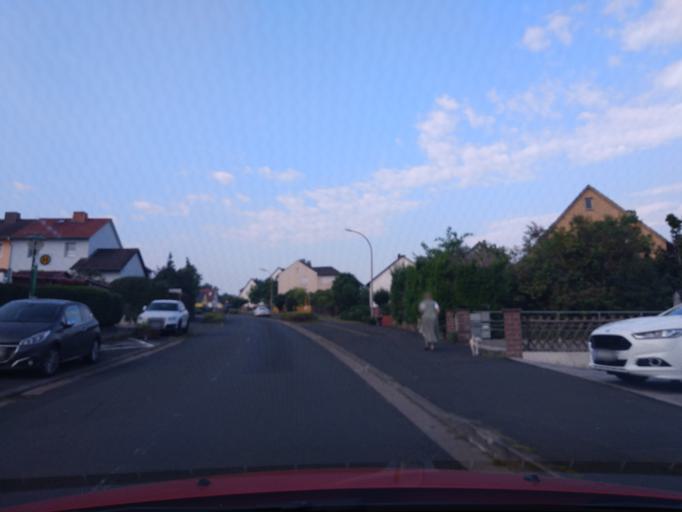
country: DE
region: Hesse
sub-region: Regierungsbezirk Kassel
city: Calden
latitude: 51.3616
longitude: 9.3858
